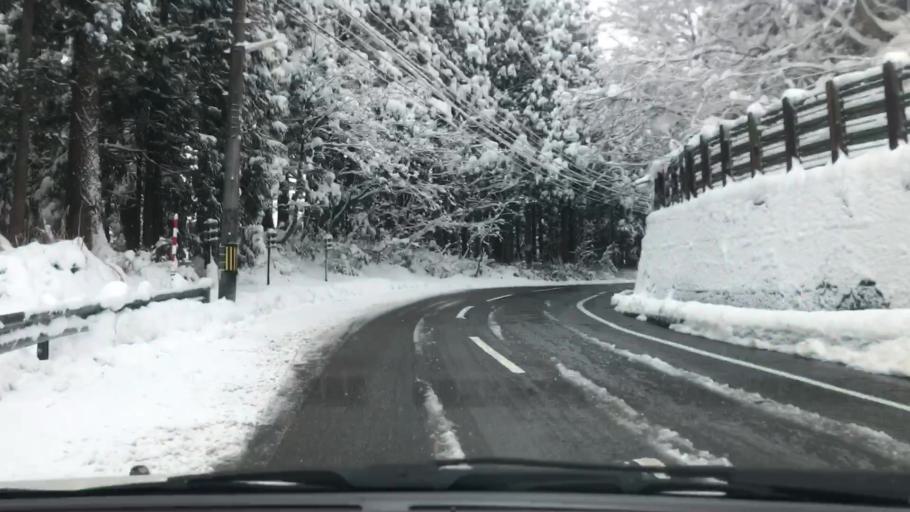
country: JP
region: Toyama
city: Kamiichi
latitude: 36.5766
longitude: 137.4054
